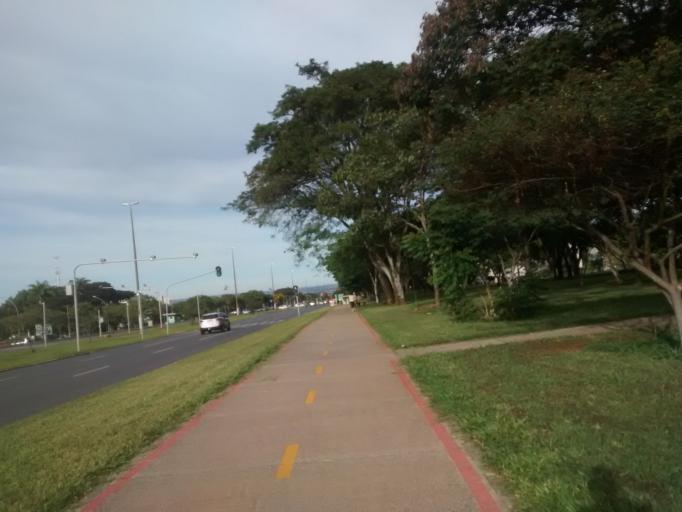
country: BR
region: Federal District
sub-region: Brasilia
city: Brasilia
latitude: -15.8130
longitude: -47.8870
